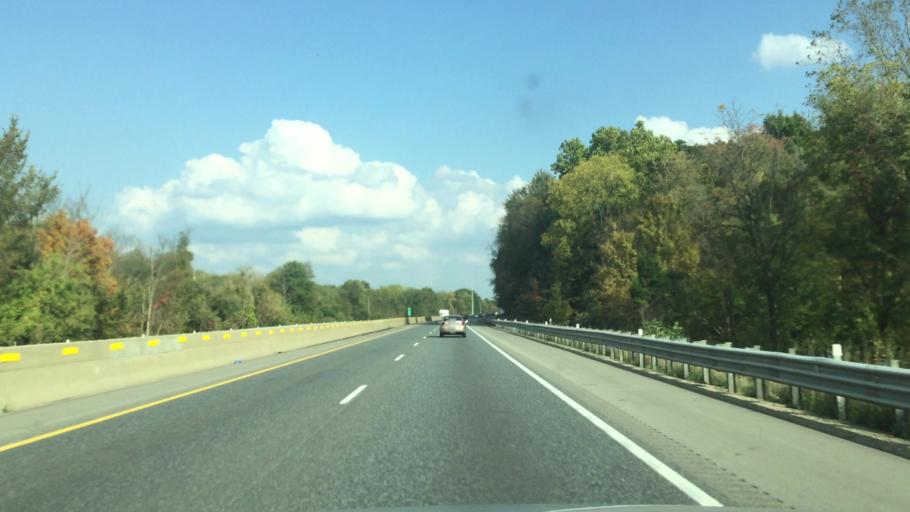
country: US
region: Michigan
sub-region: Kalamazoo County
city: Comstock Northwest
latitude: 42.2703
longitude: -85.4866
